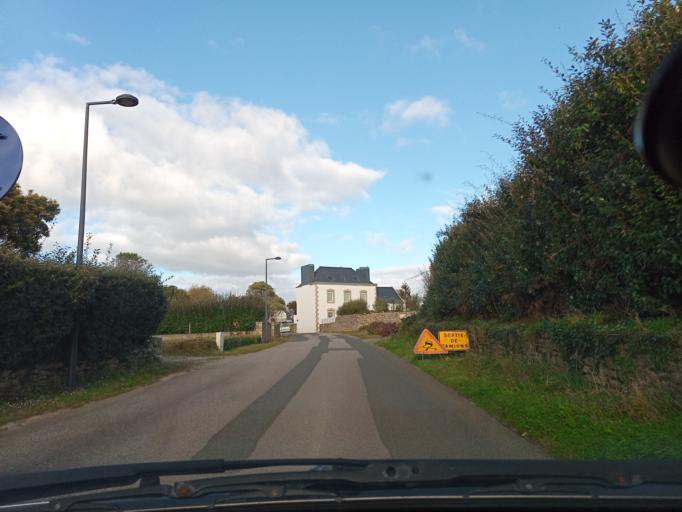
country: FR
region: Brittany
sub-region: Departement du Finistere
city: Plouhinec
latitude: 48.0127
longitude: -4.4897
